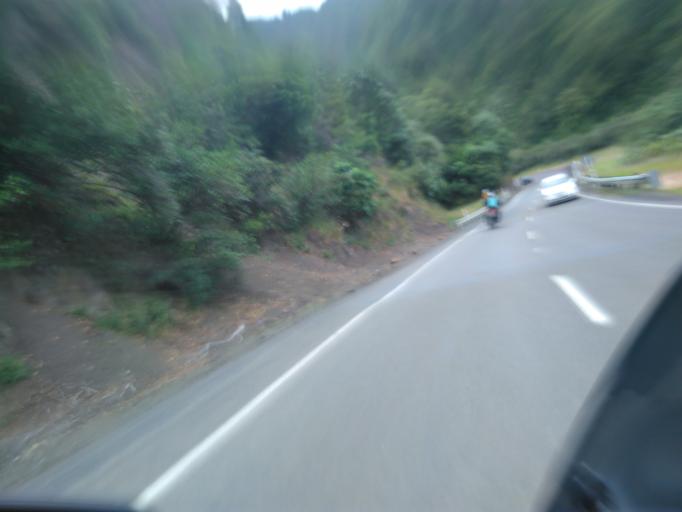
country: NZ
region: Bay of Plenty
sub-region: Opotiki District
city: Opotiki
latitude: -38.3082
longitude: 177.3948
